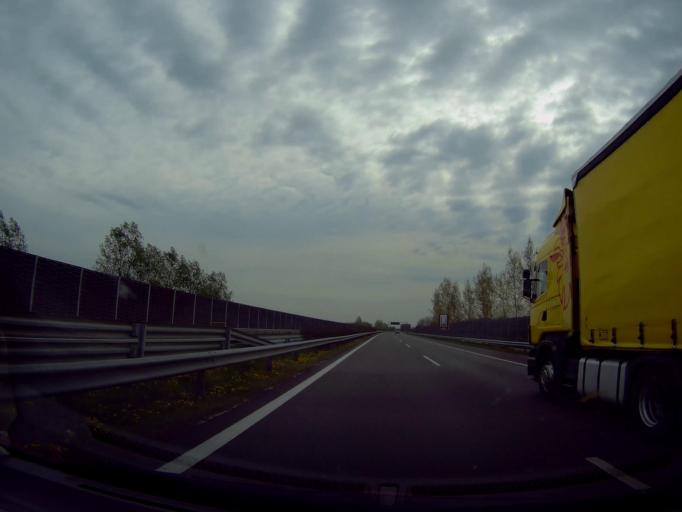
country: HU
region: Csongrad
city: Szatymaz
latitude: 46.3321
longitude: 20.0257
